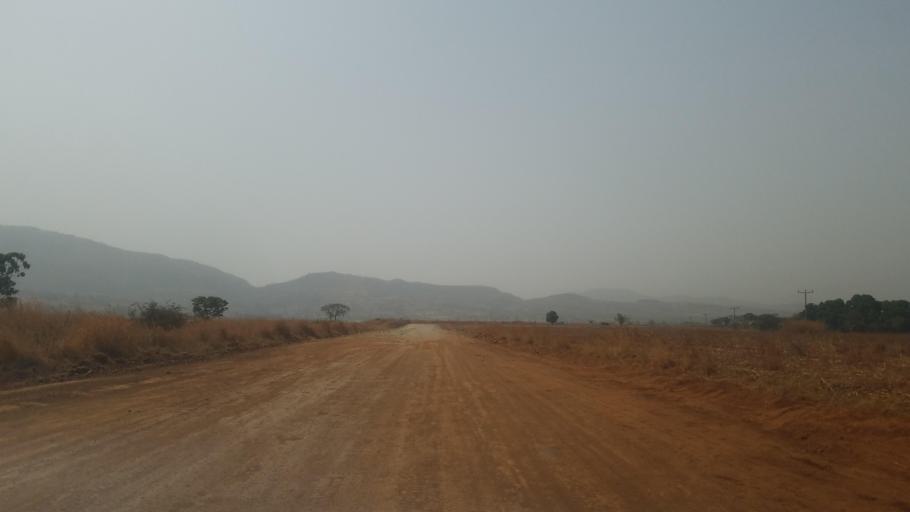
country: ET
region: Amhara
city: Bure
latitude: 10.9036
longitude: 36.4656
